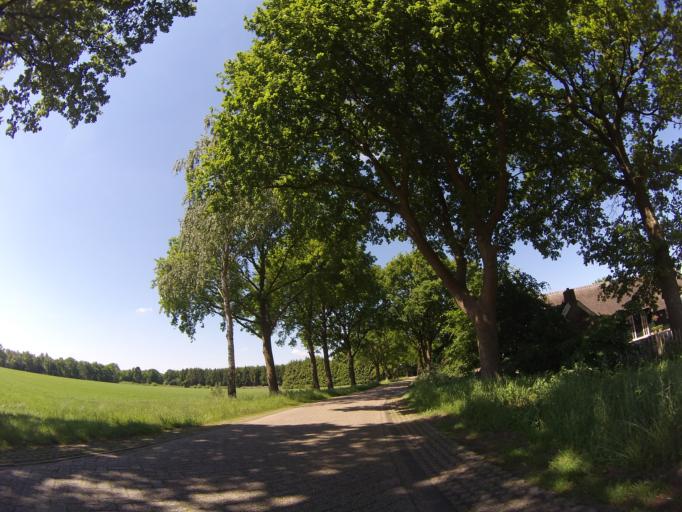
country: NL
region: Drenthe
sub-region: Gemeente Hoogeveen
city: Hoogeveen
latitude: 52.7587
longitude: 6.5461
